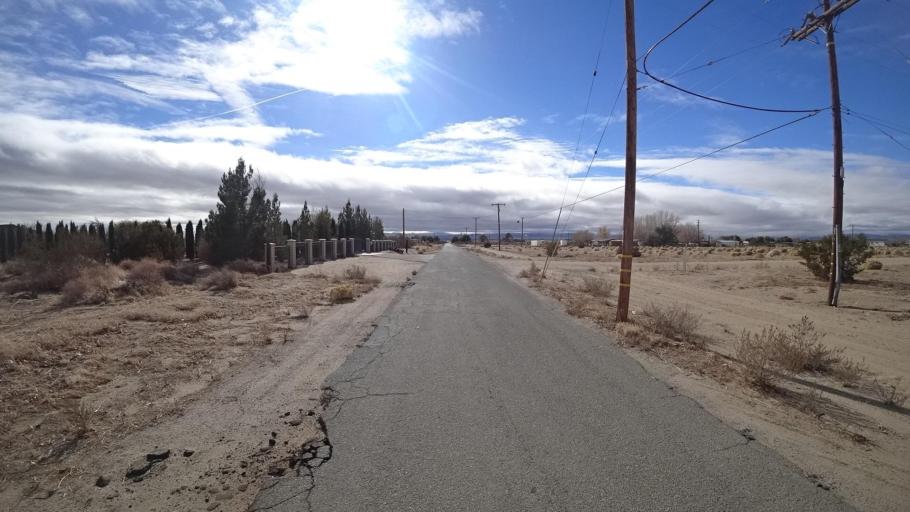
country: US
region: California
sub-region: Kern County
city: Rosamond
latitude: 34.8683
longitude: -118.2201
